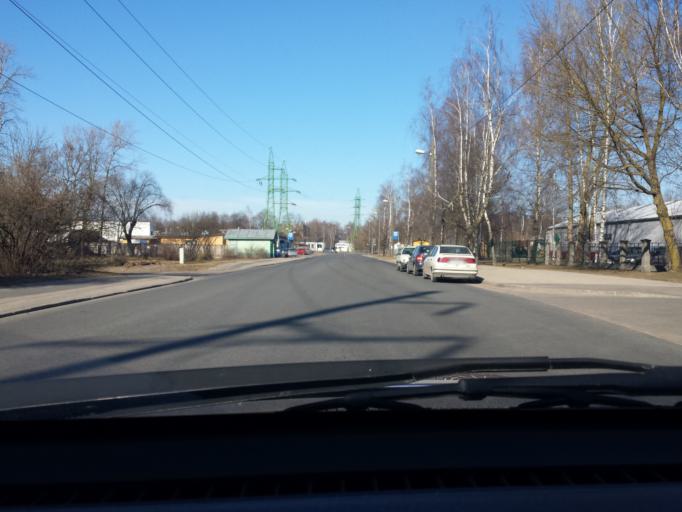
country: LV
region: Riga
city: Jaunciems
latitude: 56.9889
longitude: 24.1864
